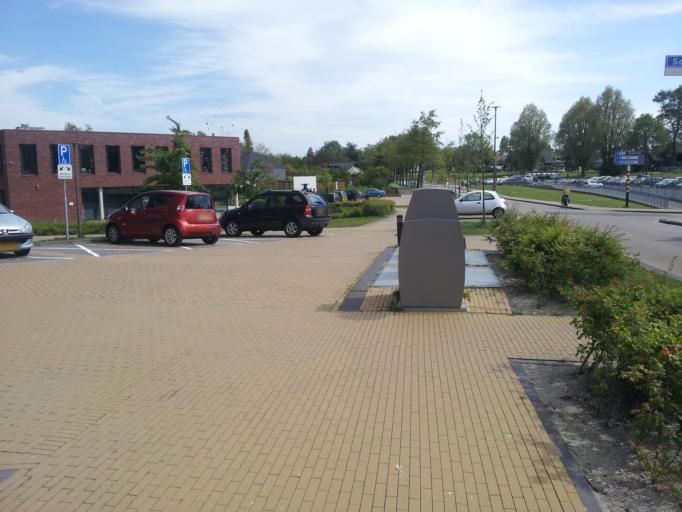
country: NL
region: South Holland
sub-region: Gemeente Zoetermeer
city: Zoetermeer
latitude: 52.0575
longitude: 4.4985
